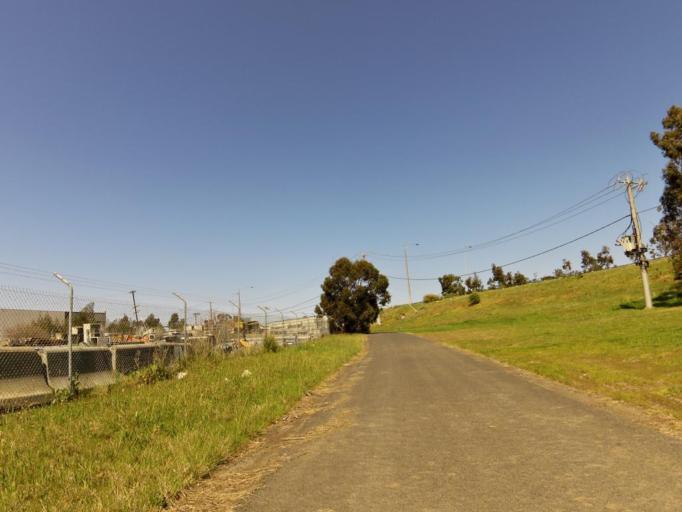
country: AU
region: Victoria
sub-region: Moonee Valley
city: Keilor East
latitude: -37.7267
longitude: 144.8640
